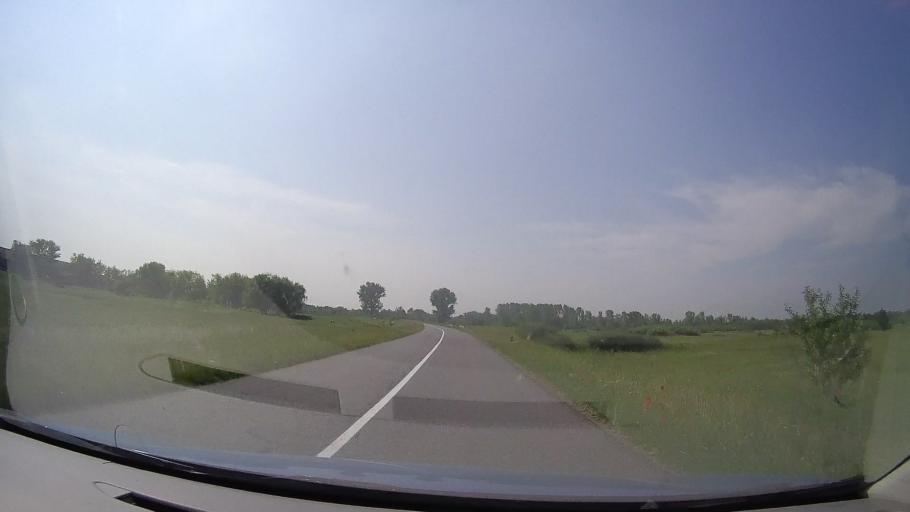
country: RS
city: Jarkovac
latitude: 45.2787
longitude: 20.7626
